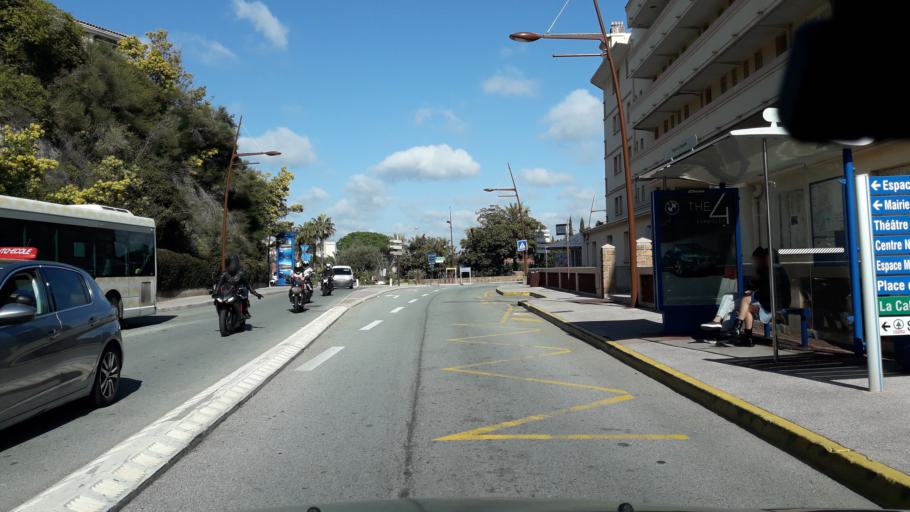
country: FR
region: Provence-Alpes-Cote d'Azur
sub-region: Departement des Alpes-Maritimes
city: Theoule-sur-Mer
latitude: 43.5223
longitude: 6.9404
